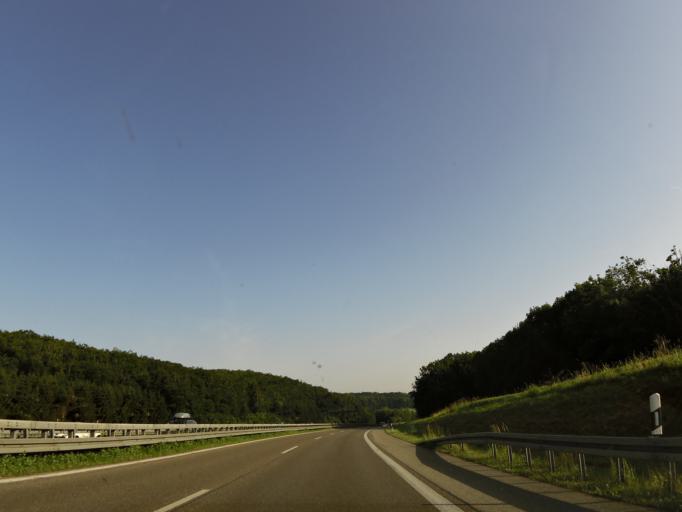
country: DE
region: Baden-Wuerttemberg
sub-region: Regierungsbezirk Stuttgart
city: Hohenstadt
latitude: 48.5375
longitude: 9.6506
